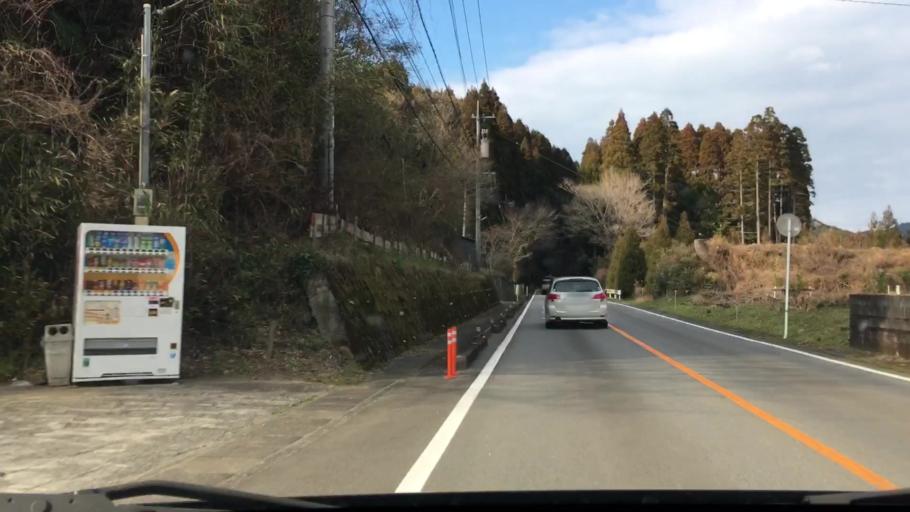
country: JP
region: Miyazaki
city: Nichinan
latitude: 31.7264
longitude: 131.3305
